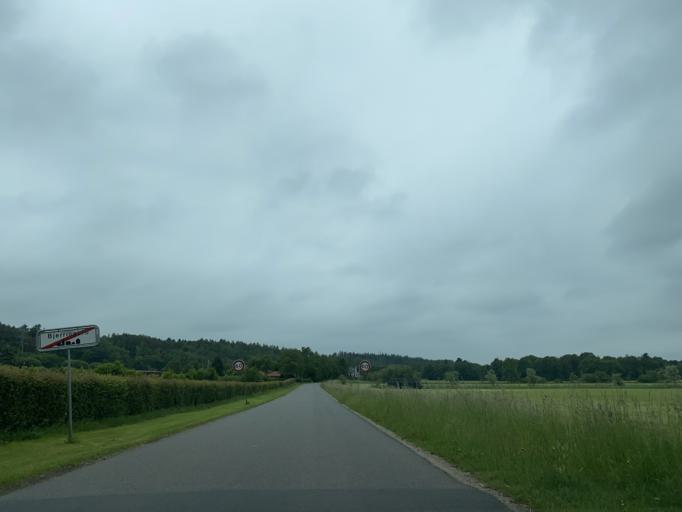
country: DK
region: Central Jutland
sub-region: Viborg Kommune
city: Bjerringbro
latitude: 56.3640
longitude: 9.6548
